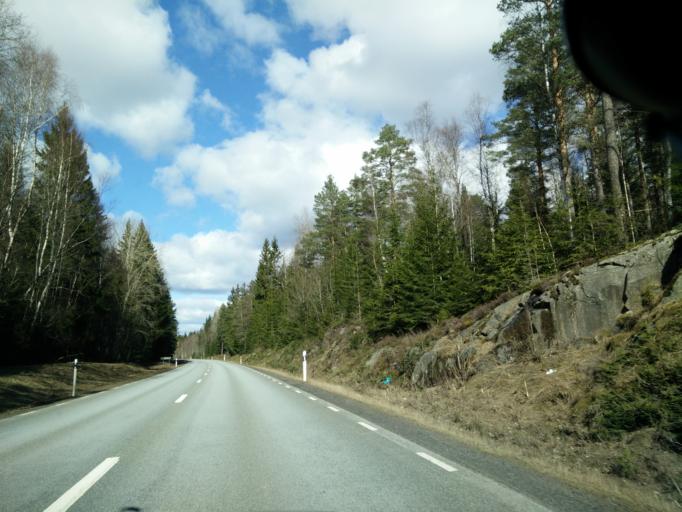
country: SE
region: Vaermland
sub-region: Munkfors Kommun
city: Munkfors
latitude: 59.8519
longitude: 13.5618
